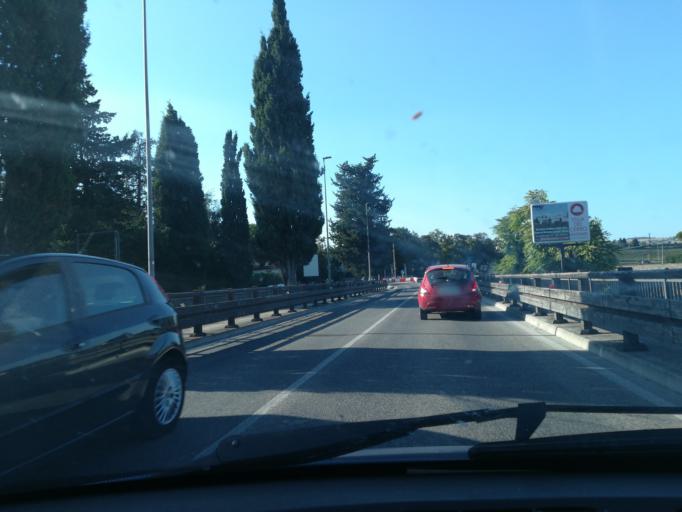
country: IT
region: The Marches
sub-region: Provincia di Macerata
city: Villa Potenza
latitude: 43.3277
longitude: 13.4256
